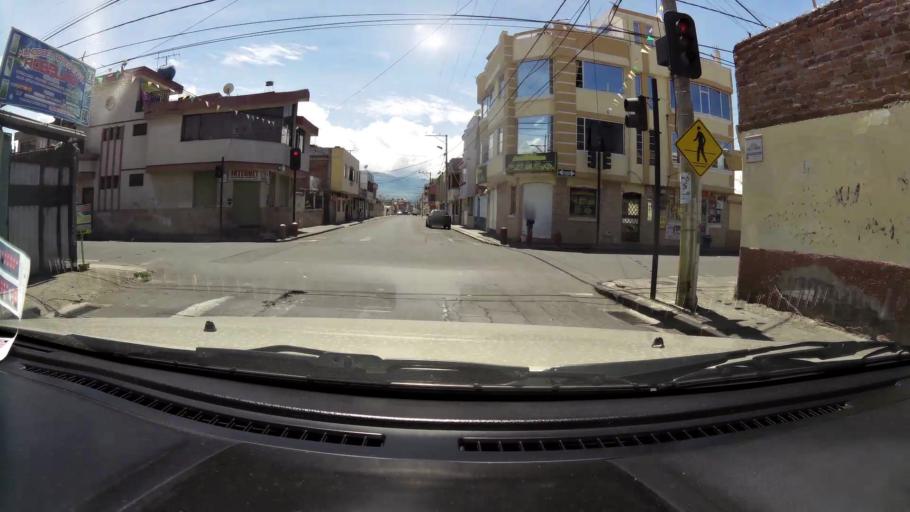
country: EC
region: Chimborazo
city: Riobamba
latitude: -1.6625
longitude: -78.6527
